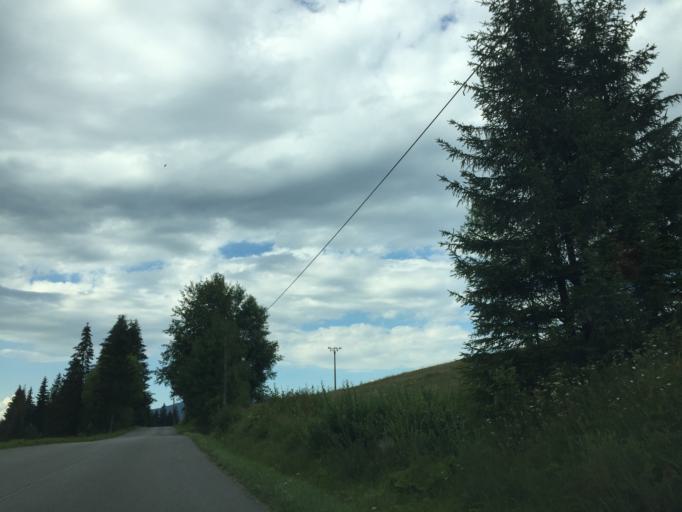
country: PL
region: Silesian Voivodeship
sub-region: Powiat zywiecki
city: Sopotnia Wielka
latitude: 49.4442
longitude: 19.3095
